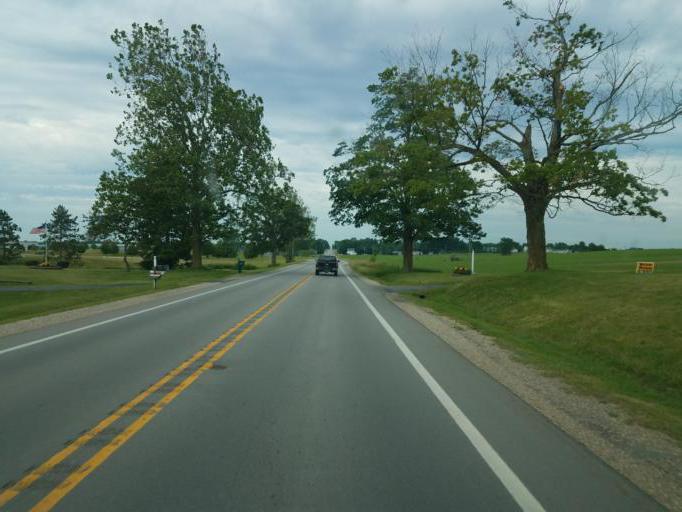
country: US
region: Michigan
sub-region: Eaton County
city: Charlotte
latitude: 42.5897
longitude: -84.8361
